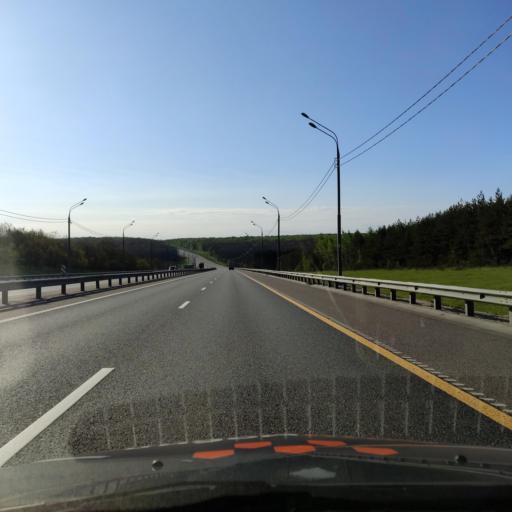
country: RU
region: Lipetsk
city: Khlevnoye
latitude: 52.2279
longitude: 39.0973
